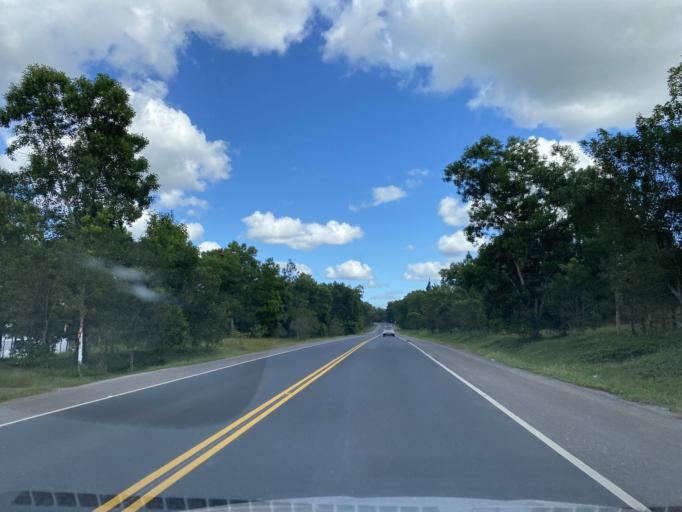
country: DO
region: Monte Plata
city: Monte Plata
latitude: 18.7793
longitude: -69.7427
